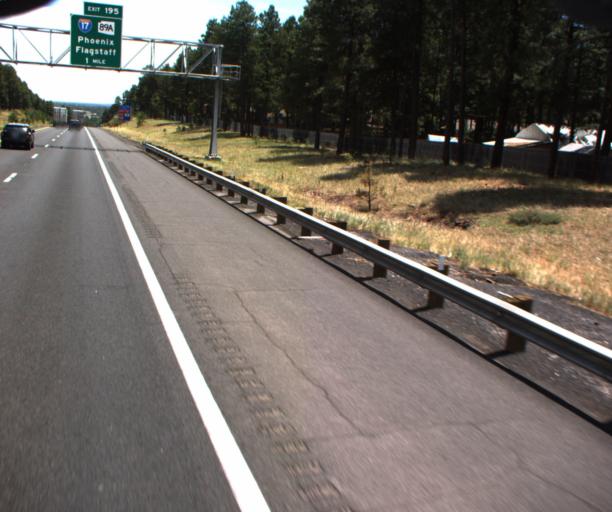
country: US
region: Arizona
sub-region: Coconino County
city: Flagstaff
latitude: 35.1782
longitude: -111.6823
